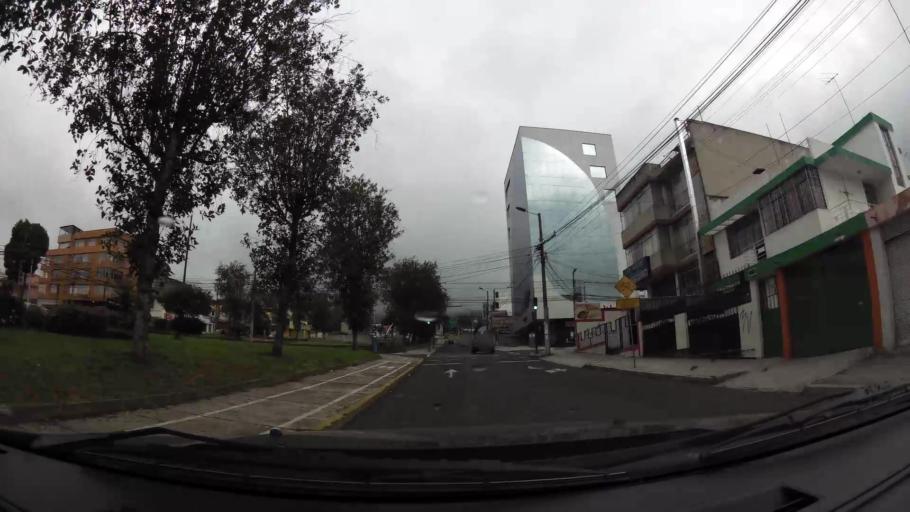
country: EC
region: Pichincha
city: Quito
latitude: -0.1872
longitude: -78.4938
